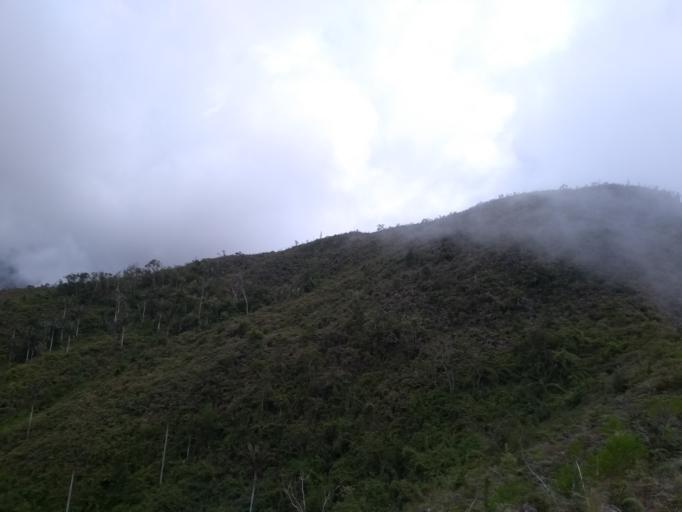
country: CO
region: Cesar
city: Manaure Balcon del Cesar
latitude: 10.1877
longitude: -73.0028
